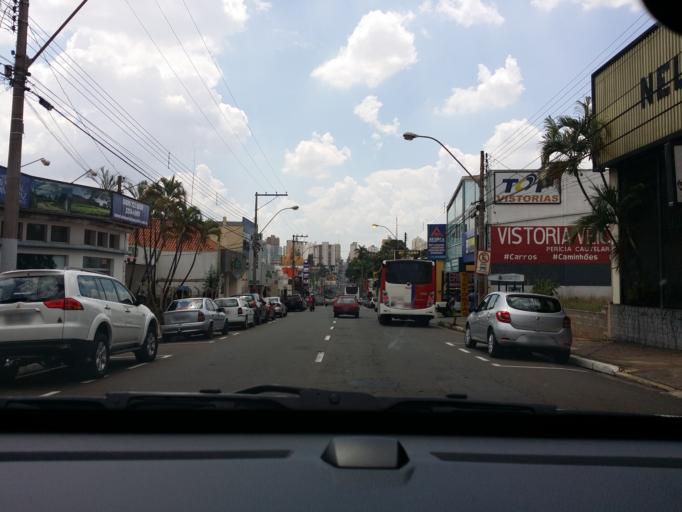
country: BR
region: Sao Paulo
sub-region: Sao Carlos
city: Sao Carlos
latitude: -22.0254
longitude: -47.8906
